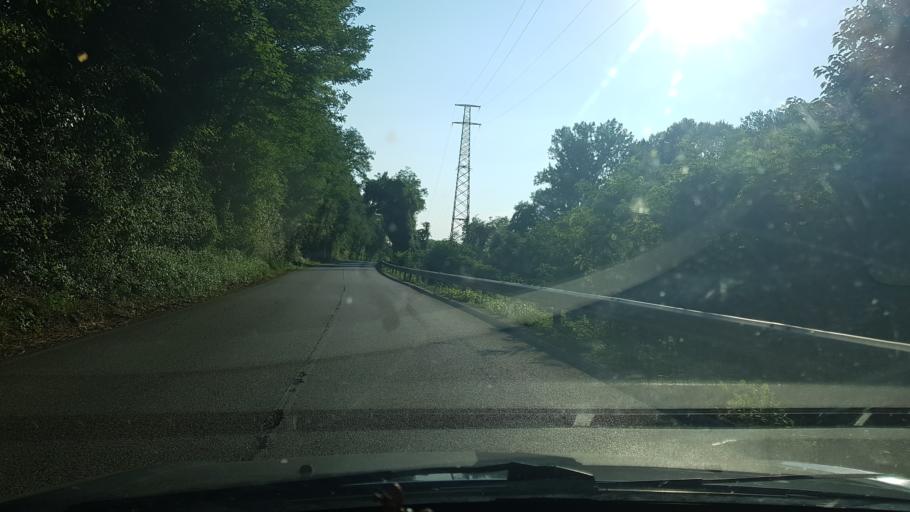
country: IT
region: Friuli Venezia Giulia
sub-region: Provincia di Gorizia
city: Farra d'Isonzo
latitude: 45.8917
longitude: 13.5225
